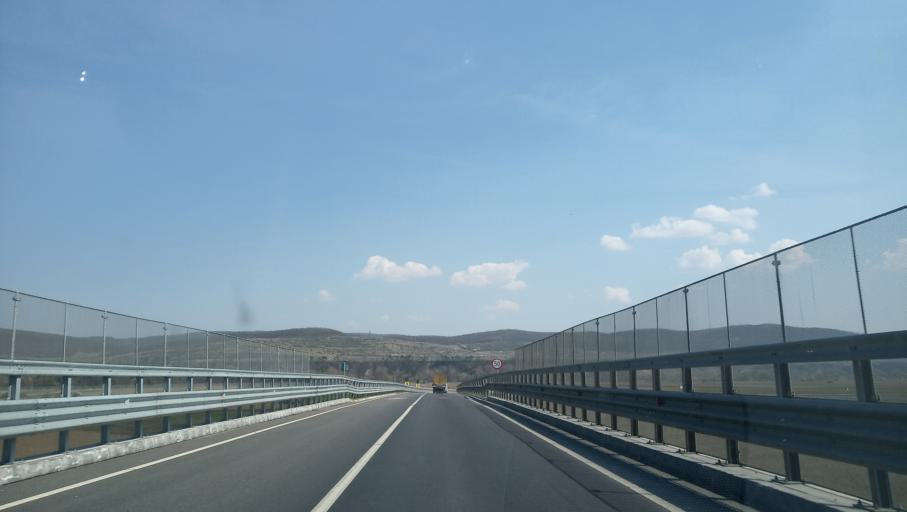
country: RO
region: Alba
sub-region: Municipiul Aiud
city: Aiud
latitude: 46.3295
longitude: 23.7290
